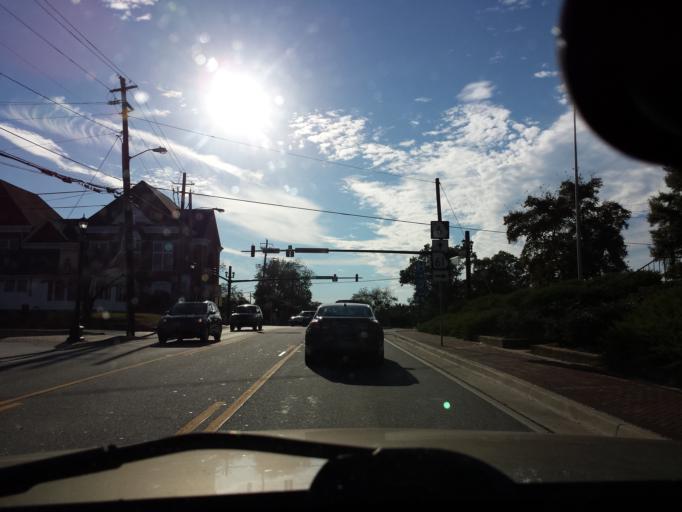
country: US
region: Georgia
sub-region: Paulding County
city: Dallas
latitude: 33.9247
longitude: -84.8406
